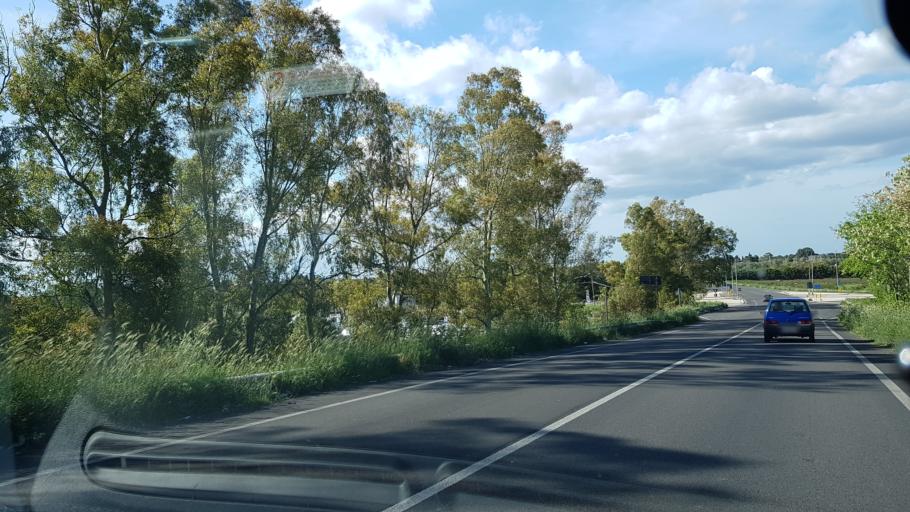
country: IT
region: Apulia
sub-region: Provincia di Brindisi
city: Mesagne
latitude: 40.5606
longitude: 17.7878
